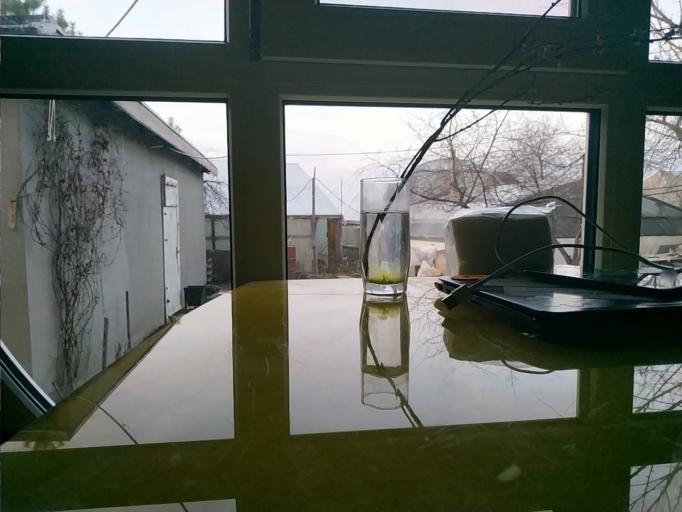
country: RU
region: Republic of Karelia
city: Sukkozero
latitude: 62.6264
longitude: 31.9234
